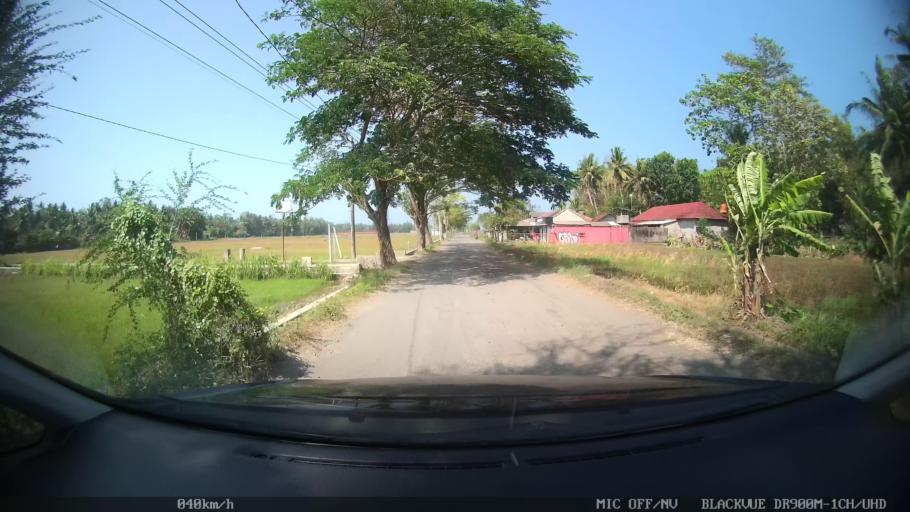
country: ID
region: Daerah Istimewa Yogyakarta
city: Srandakan
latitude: -7.9527
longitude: 110.2184
